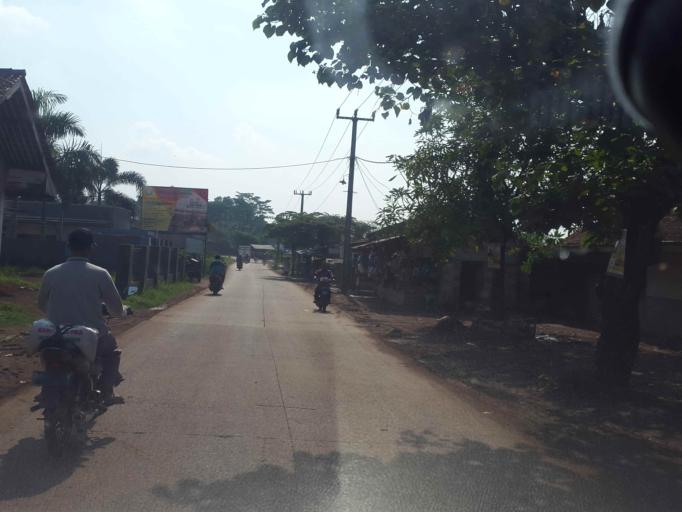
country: ID
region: West Java
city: Cileungsir
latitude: -6.3391
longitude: 107.0457
